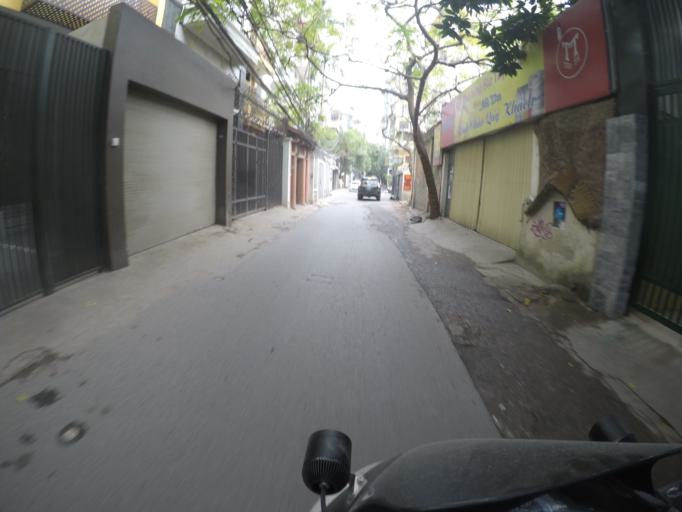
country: VN
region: Ha Noi
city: Tay Ho
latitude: 21.0702
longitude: 105.8232
